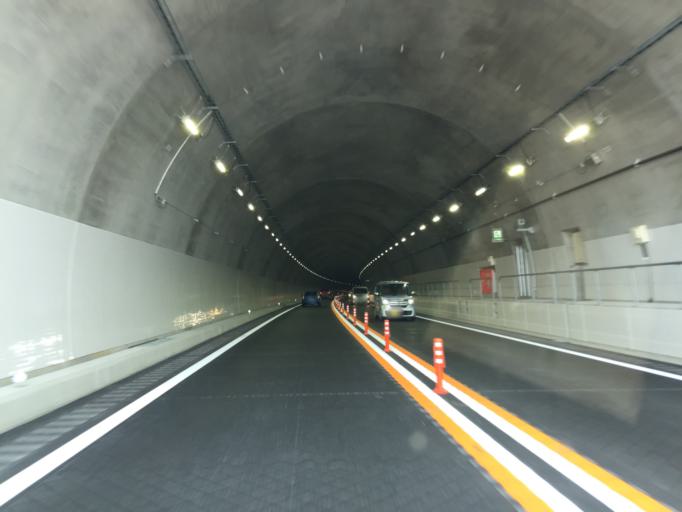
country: JP
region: Yamagata
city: Kaminoyama
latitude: 38.1597
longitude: 140.3075
